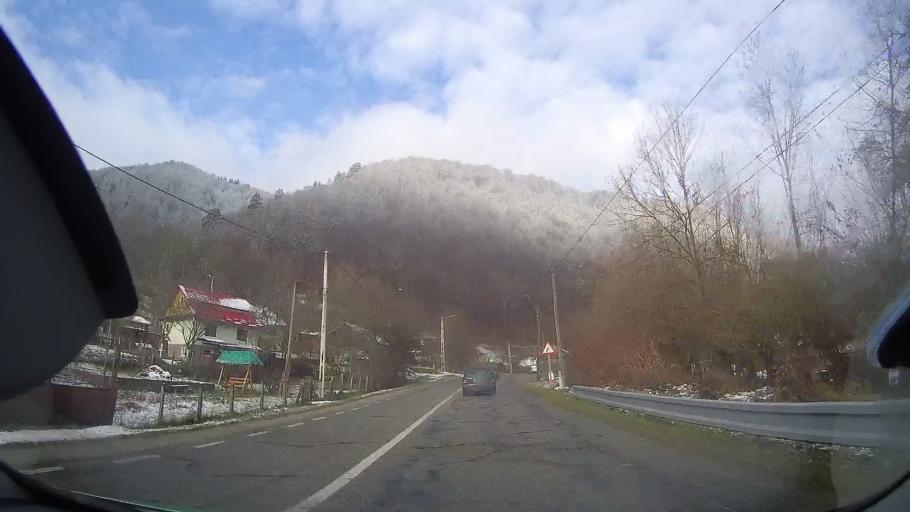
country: RO
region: Alba
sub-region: Oras Baia de Aries
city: Baia de Aries
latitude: 46.3856
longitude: 23.2806
